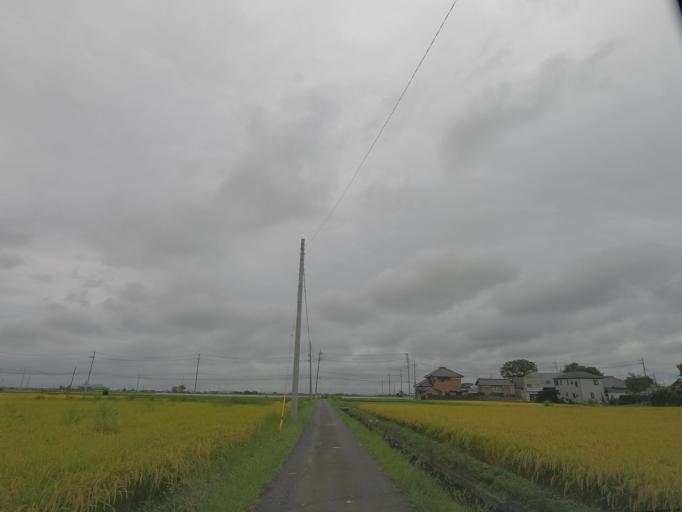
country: JP
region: Ibaraki
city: Toride
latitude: 35.9281
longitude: 140.0560
